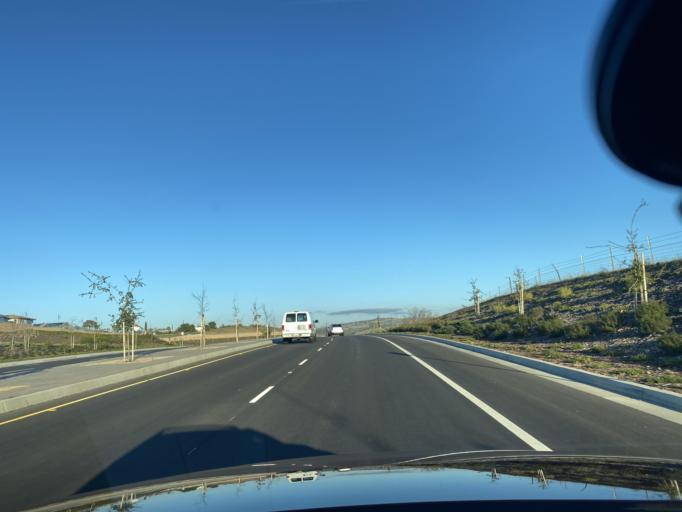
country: US
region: California
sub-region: El Dorado County
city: El Dorado Hills
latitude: 38.6489
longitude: -121.0843
